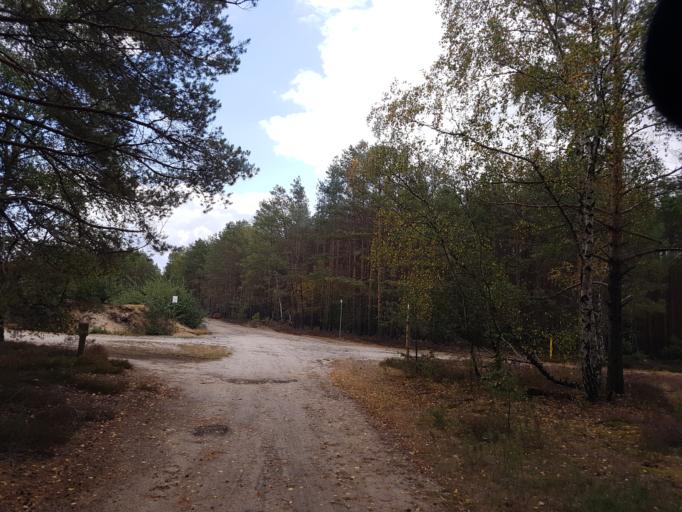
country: DE
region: Brandenburg
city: Finsterwalde
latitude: 51.5881
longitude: 13.7565
